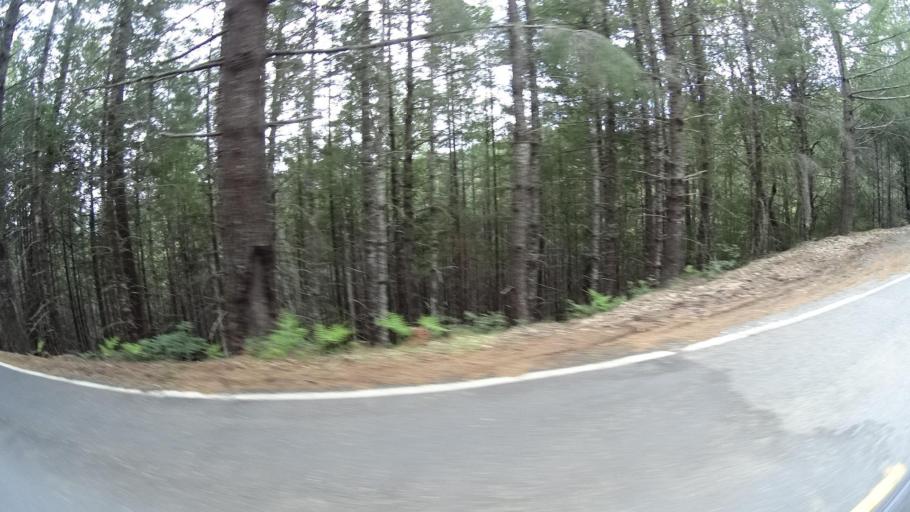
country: US
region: California
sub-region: Humboldt County
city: Redway
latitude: 40.0490
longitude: -124.0165
